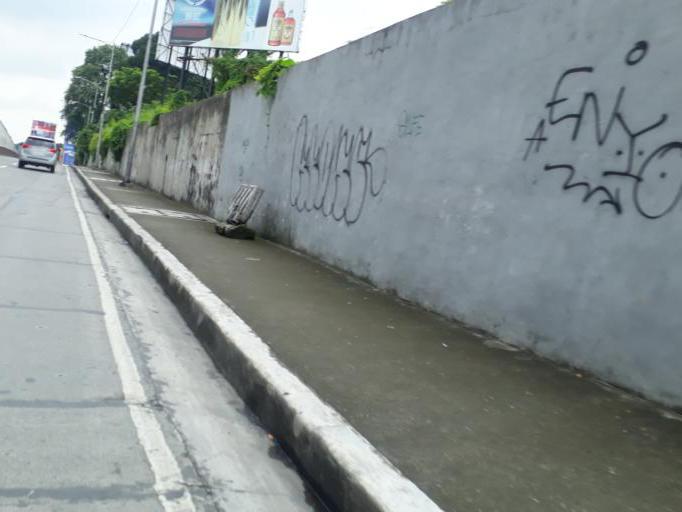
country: PH
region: Metro Manila
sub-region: Marikina
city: Calumpang
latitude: 14.6303
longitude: 121.0741
